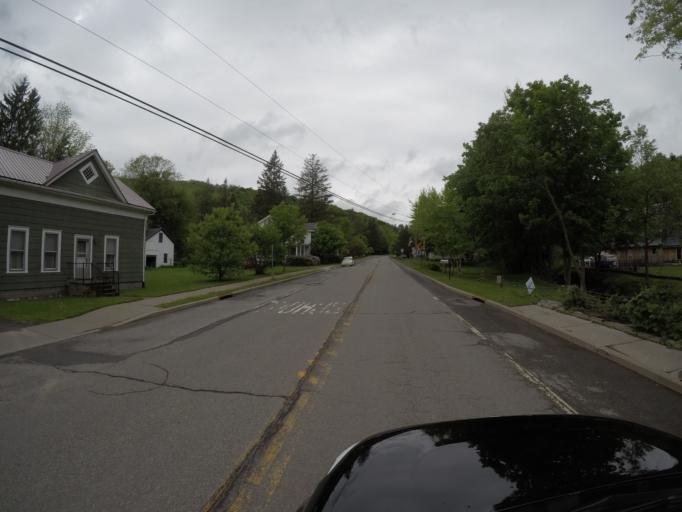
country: US
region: New York
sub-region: Delaware County
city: Delhi
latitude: 42.1906
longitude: -74.7871
